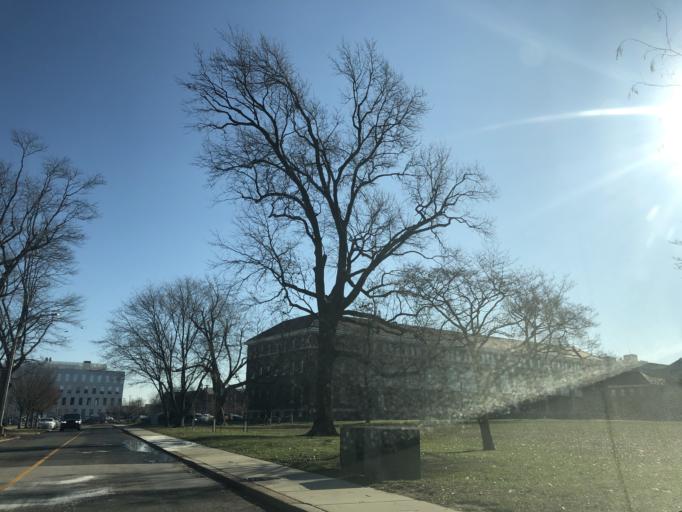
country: US
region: New Jersey
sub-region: Gloucester County
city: National Park
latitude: 39.8939
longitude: -75.1757
